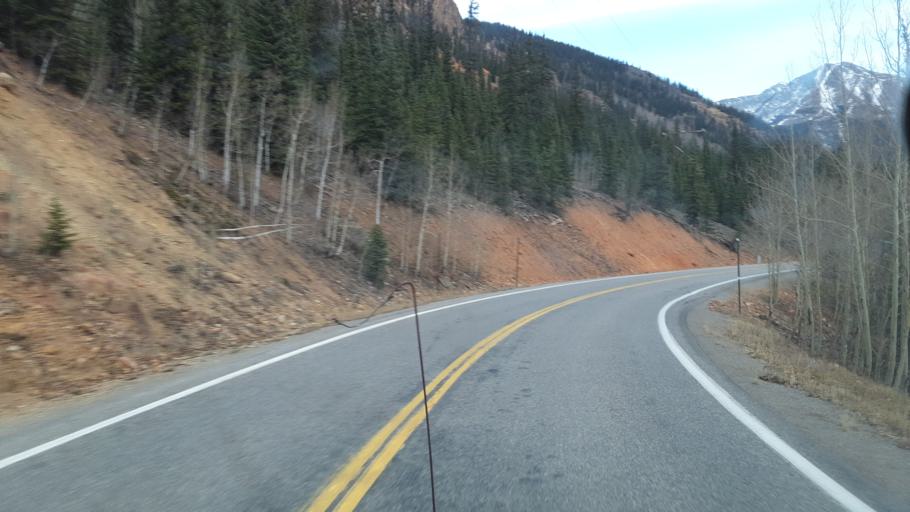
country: US
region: Colorado
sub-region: San Juan County
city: Silverton
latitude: 37.8198
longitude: -107.7051
